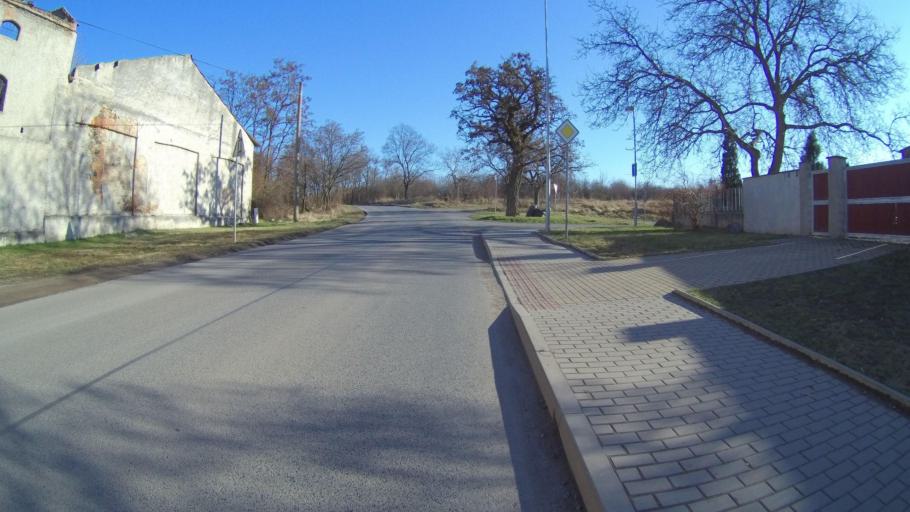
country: CZ
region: Central Bohemia
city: Neratovice
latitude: 50.2371
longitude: 14.5101
